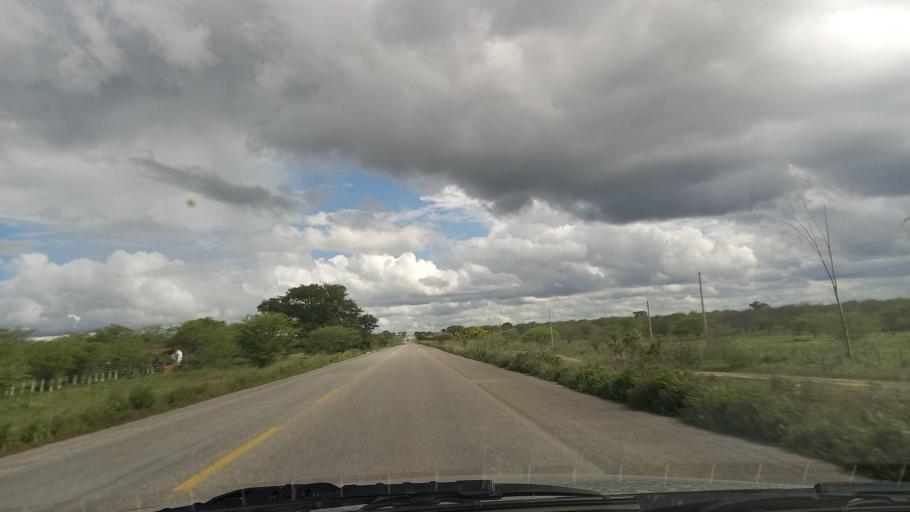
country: BR
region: Pernambuco
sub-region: Cachoeirinha
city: Cachoeirinha
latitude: -8.5119
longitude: -36.2525
